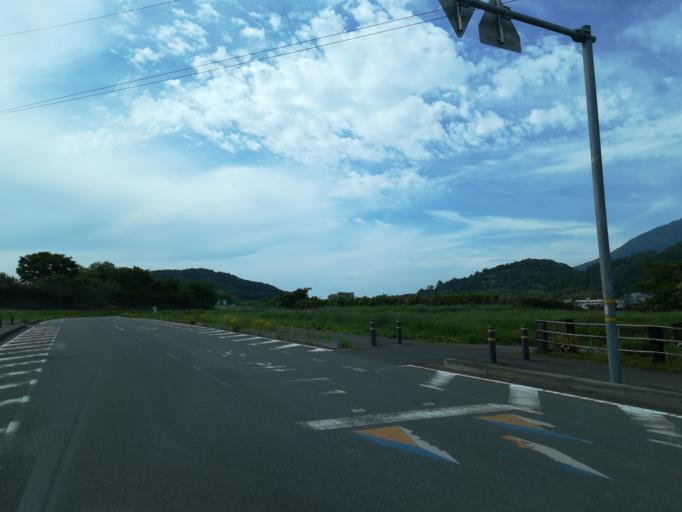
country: JP
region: Ibaraki
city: Tsukuba
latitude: 36.1759
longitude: 140.1026
